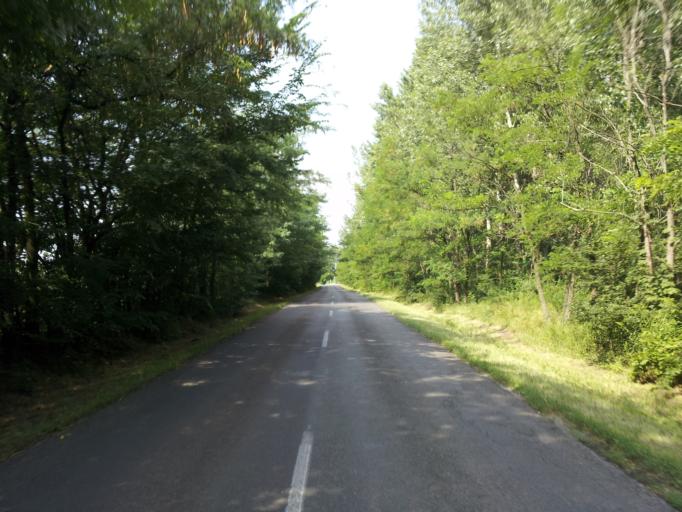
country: HU
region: Pest
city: Szigetcsep
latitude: 47.2417
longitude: 18.9629
